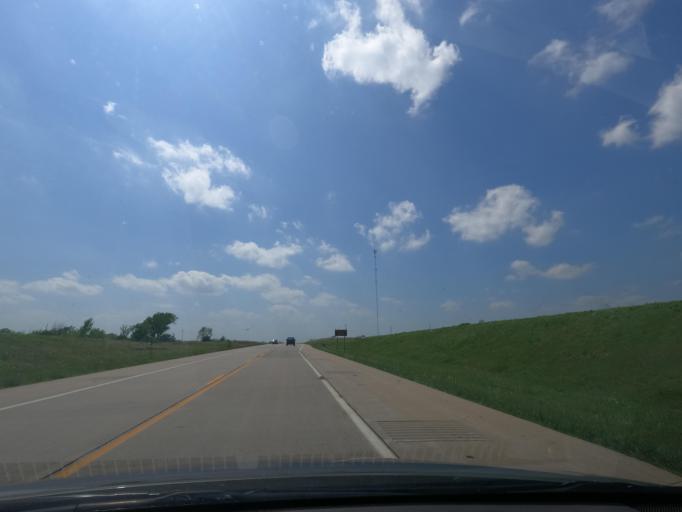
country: US
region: Kansas
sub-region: Elk County
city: Howard
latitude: 37.6277
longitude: -96.0949
